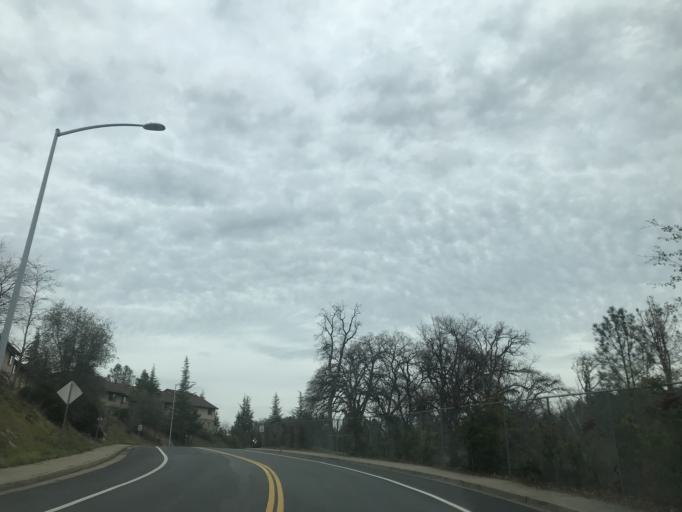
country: US
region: California
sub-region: El Dorado County
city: Placerville
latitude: 38.7284
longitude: -120.8329
